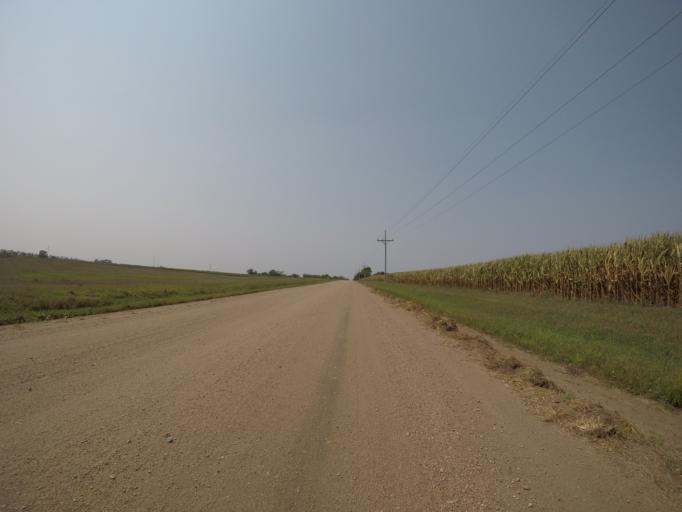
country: US
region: Nebraska
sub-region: Gage County
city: Beatrice
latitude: 40.2774
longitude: -96.7963
